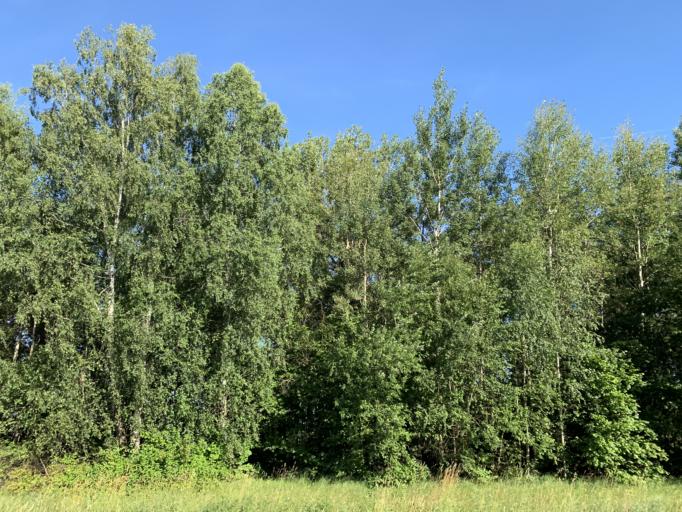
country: BY
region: Minsk
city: Novy Svyerzhan'
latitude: 53.4147
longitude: 26.6474
